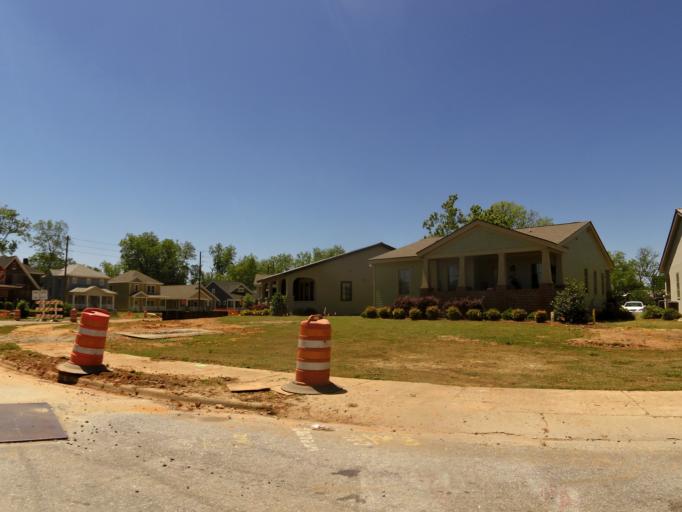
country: US
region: Georgia
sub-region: Richmond County
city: Augusta
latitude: 33.4598
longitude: -81.9763
